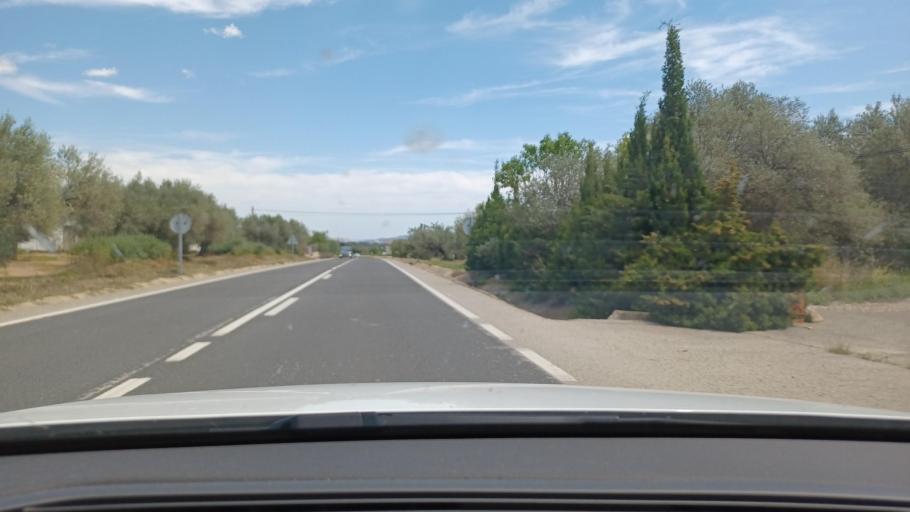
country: ES
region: Valencia
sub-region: Provincia de Castello
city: Rosell
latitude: 40.6304
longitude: 0.2986
